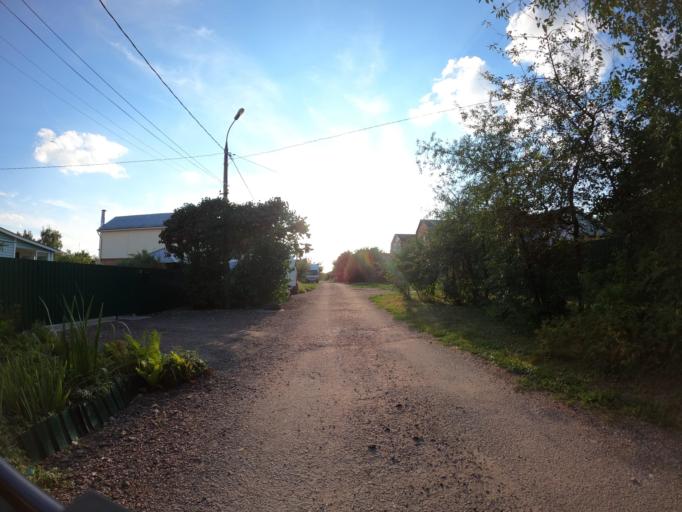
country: RU
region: Moskovskaya
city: Raduzhnyy
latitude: 55.1073
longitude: 38.7298
